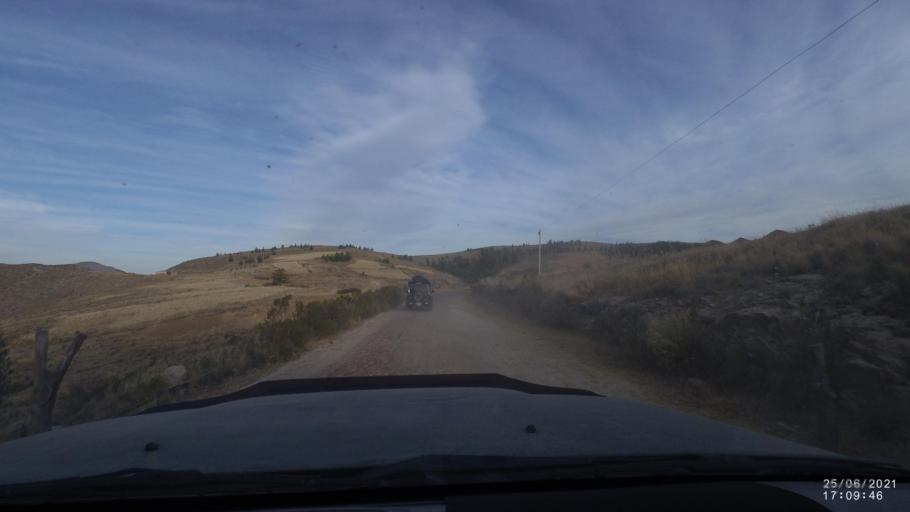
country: BO
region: Cochabamba
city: Arani
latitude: -17.8371
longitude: -65.7030
